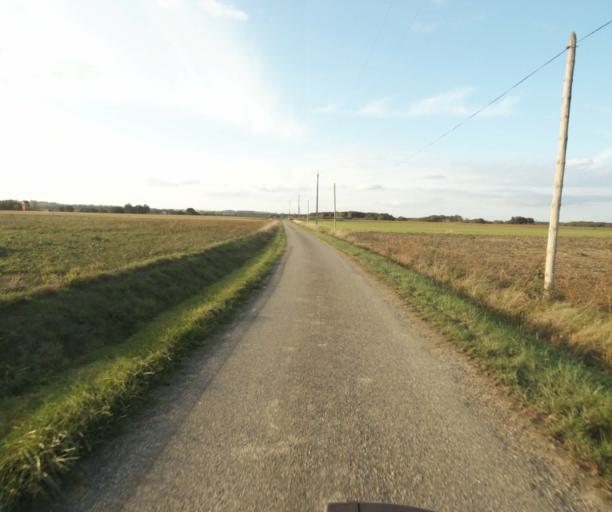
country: FR
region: Midi-Pyrenees
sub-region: Departement du Tarn-et-Garonne
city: Verdun-sur-Garonne
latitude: 43.8289
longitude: 1.1541
